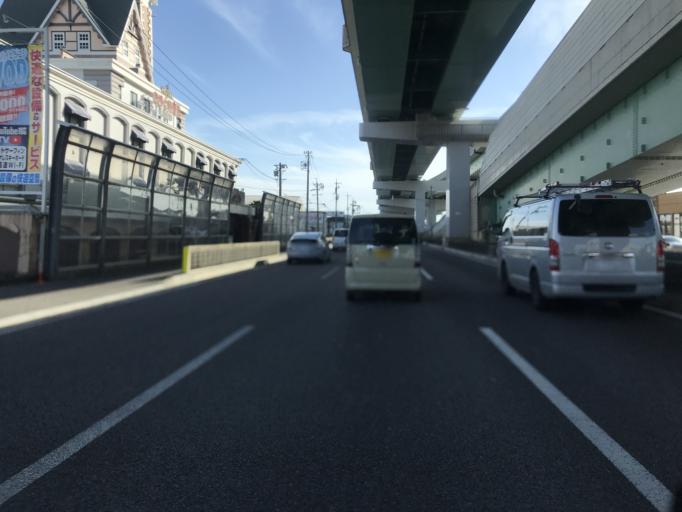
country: JP
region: Aichi
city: Iwakura
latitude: 35.2367
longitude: 136.8489
